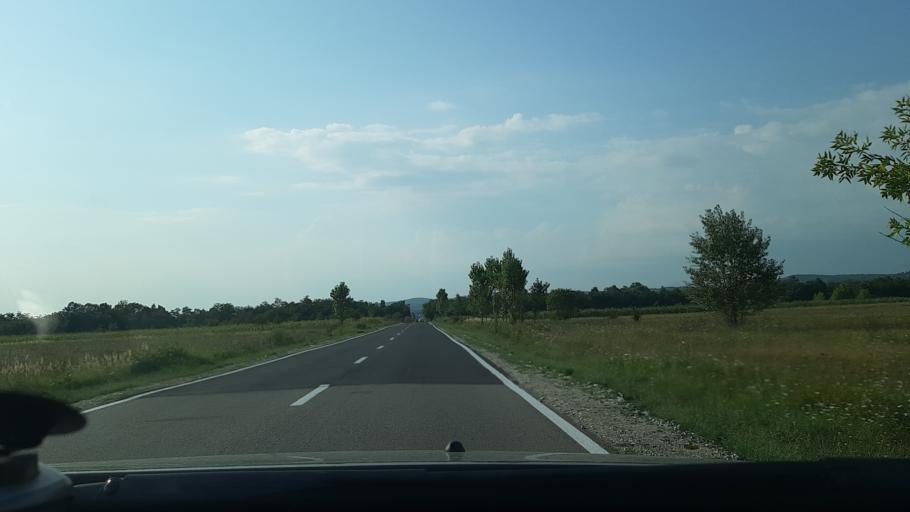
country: RO
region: Gorj
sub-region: Comuna Targu Carbunesti
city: Pojogeni
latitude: 45.0052
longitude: 23.4850
